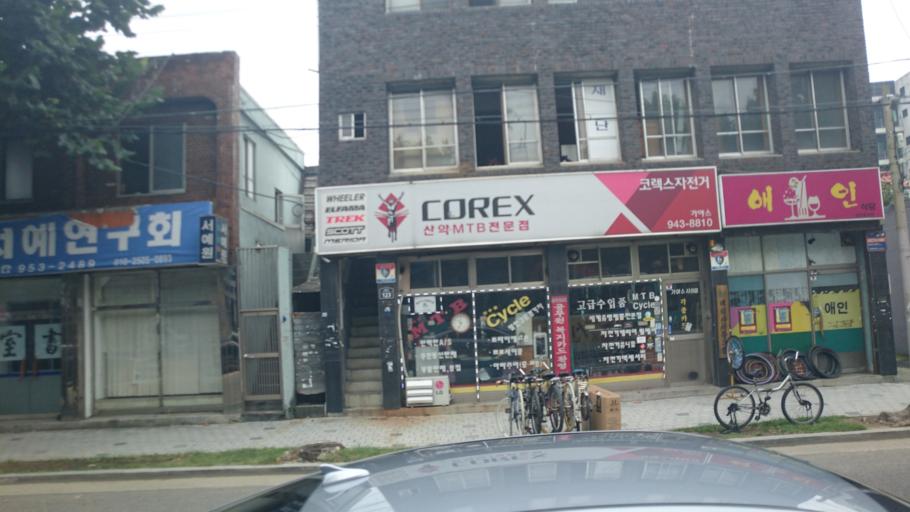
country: KR
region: Daegu
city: Daegu
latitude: 35.8870
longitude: 128.6412
